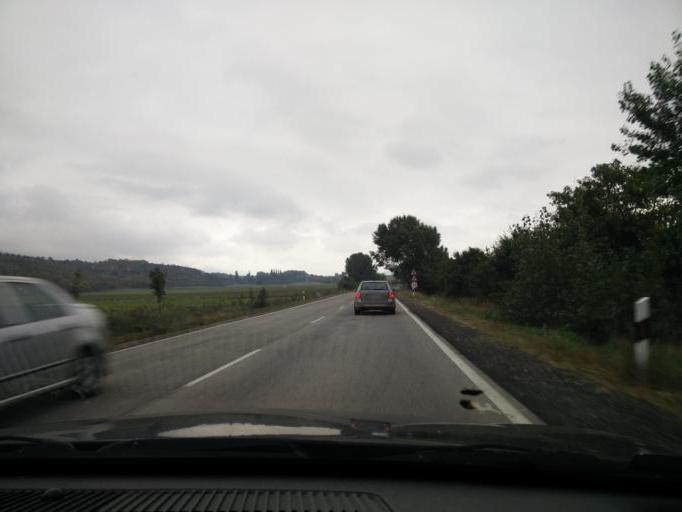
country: HU
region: Komarom-Esztergom
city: Dorog
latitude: 47.7276
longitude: 18.7614
